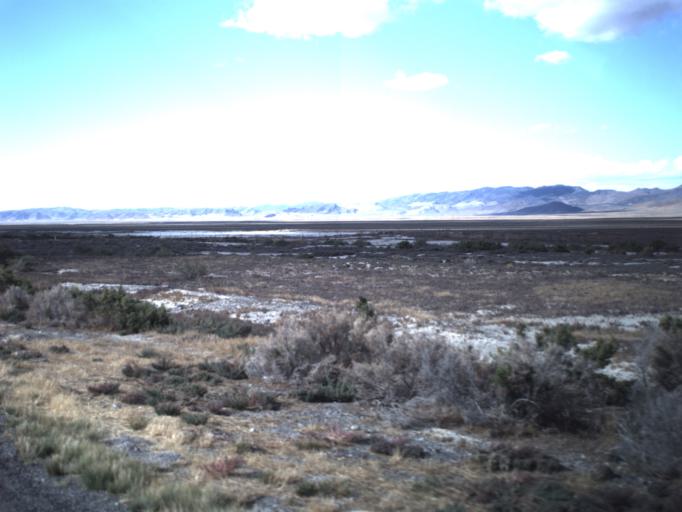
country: US
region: Utah
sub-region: Millard County
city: Delta
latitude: 39.0330
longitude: -112.7744
